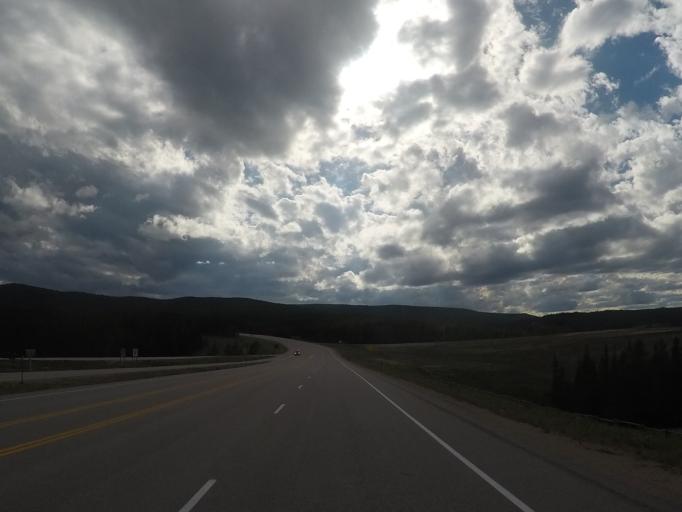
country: US
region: Wyoming
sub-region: Sheridan County
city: Sheridan
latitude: 44.7907
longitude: -107.3930
